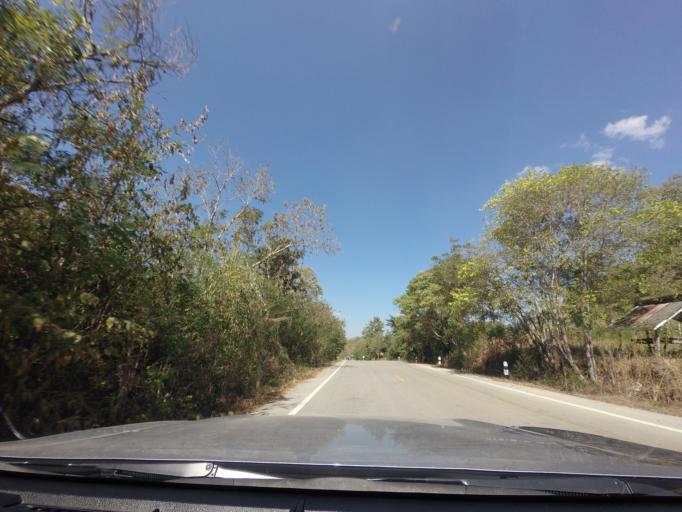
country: TH
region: Lampang
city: Chae Hom
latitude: 18.5872
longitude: 99.6266
